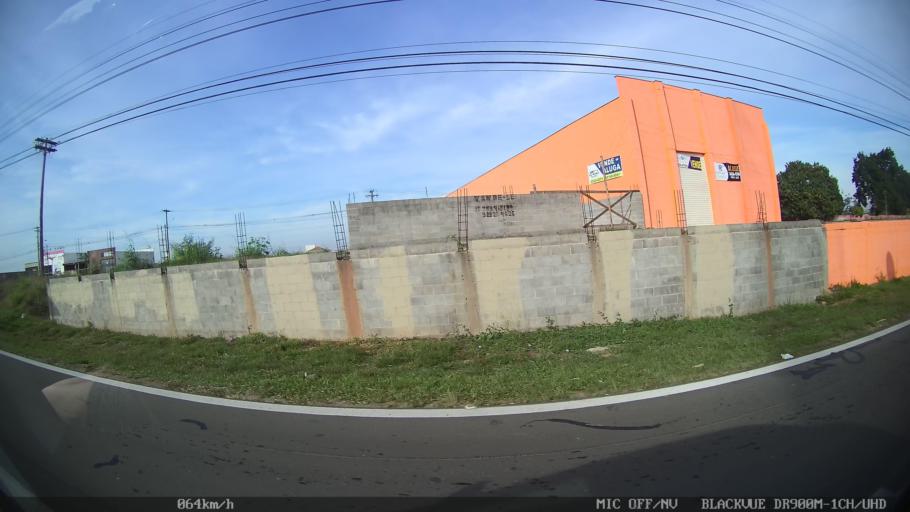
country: BR
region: Sao Paulo
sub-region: Piracicaba
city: Piracicaba
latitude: -22.6790
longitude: -47.7115
